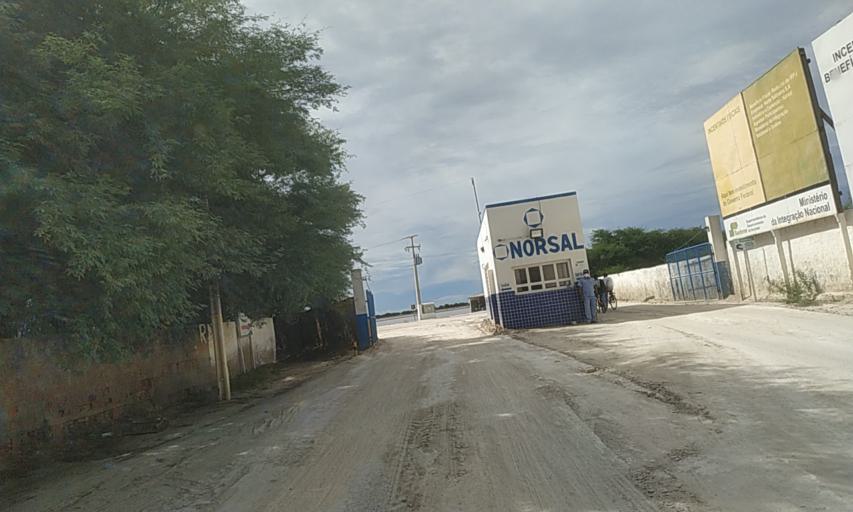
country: BR
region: Rio Grande do Norte
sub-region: Areia Branca
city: Areia Branca
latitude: -4.9497
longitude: -37.1332
